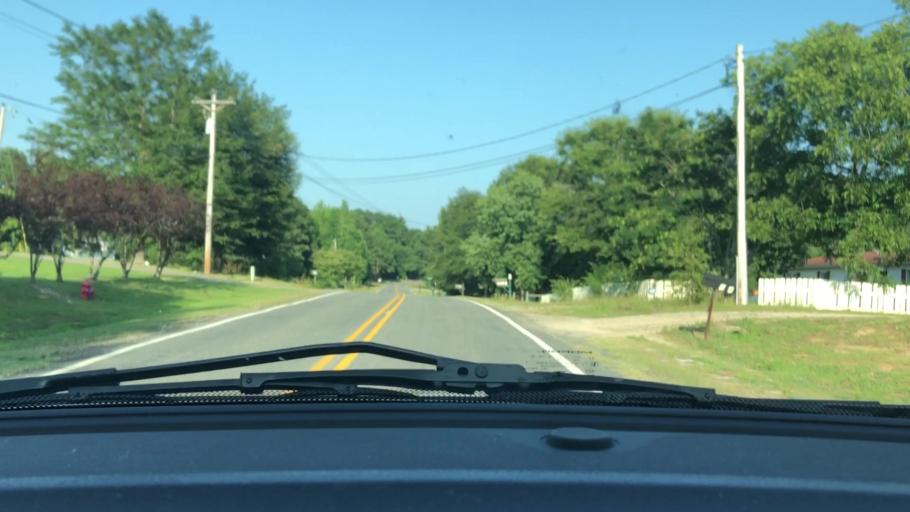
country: US
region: North Carolina
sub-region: Lee County
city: Broadway
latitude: 35.3273
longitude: -79.0568
